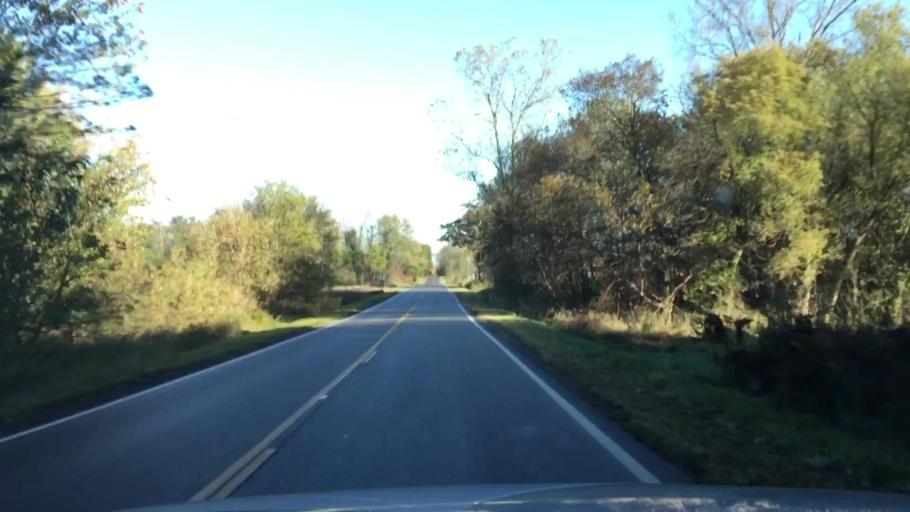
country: US
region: Michigan
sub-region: Genesee County
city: Argentine
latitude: 42.7647
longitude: -83.9414
